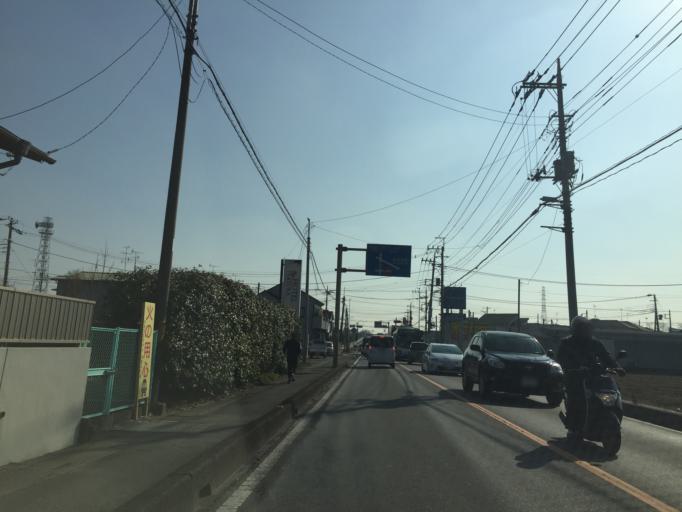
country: JP
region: Saitama
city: Shiki
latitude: 35.8353
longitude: 139.5987
